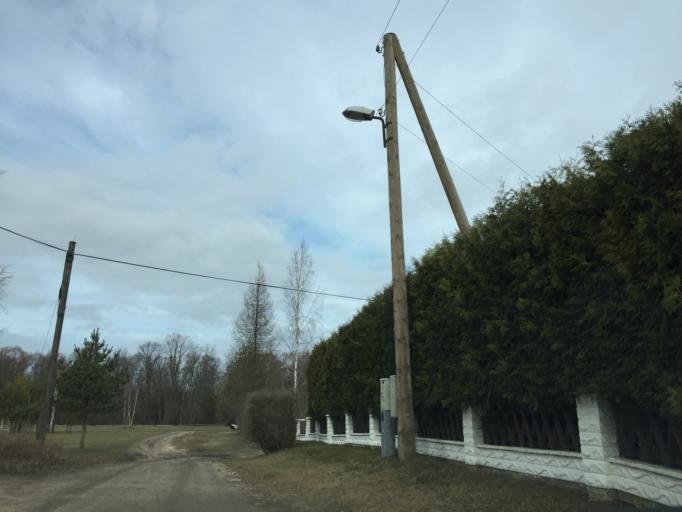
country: LV
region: Garkalne
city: Garkalne
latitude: 57.0735
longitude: 24.4194
